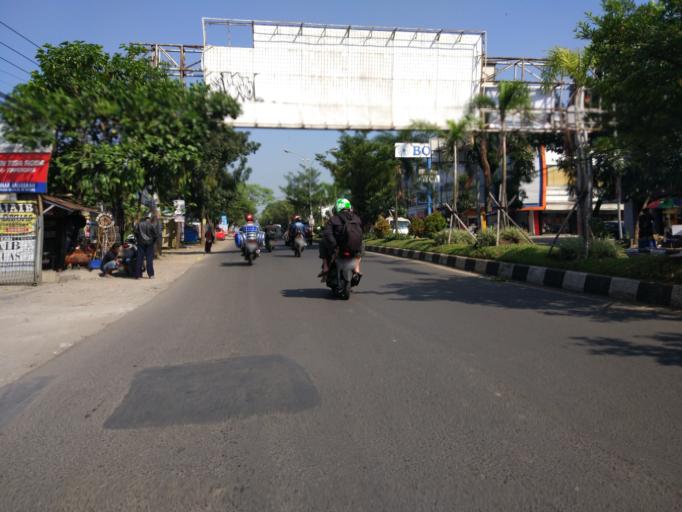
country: ID
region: West Java
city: Bandung
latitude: -6.9130
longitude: 107.6497
